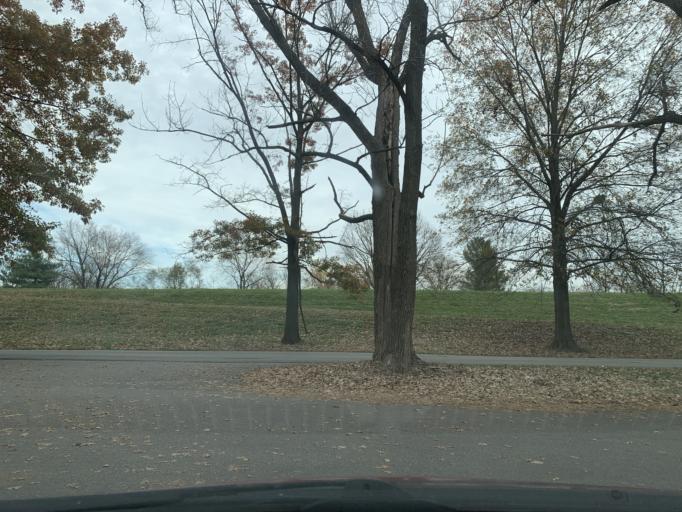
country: US
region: Kentucky
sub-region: Jefferson County
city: Louisville
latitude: 38.2747
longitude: -85.7618
